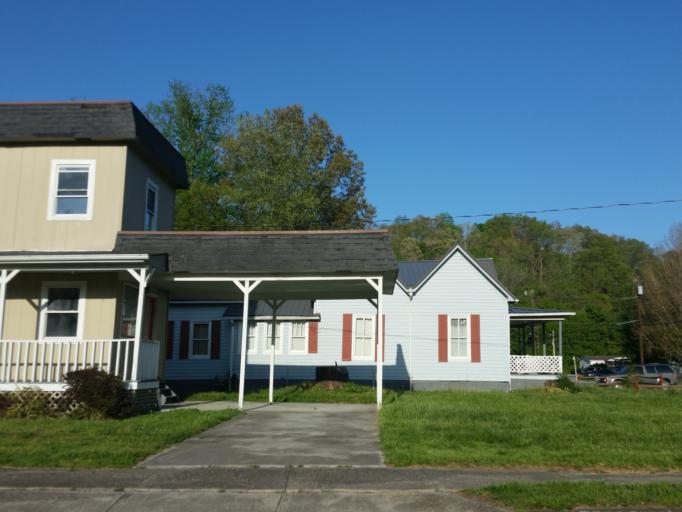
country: US
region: Kentucky
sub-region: Bell County
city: Middlesboro
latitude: 36.6039
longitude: -83.7154
